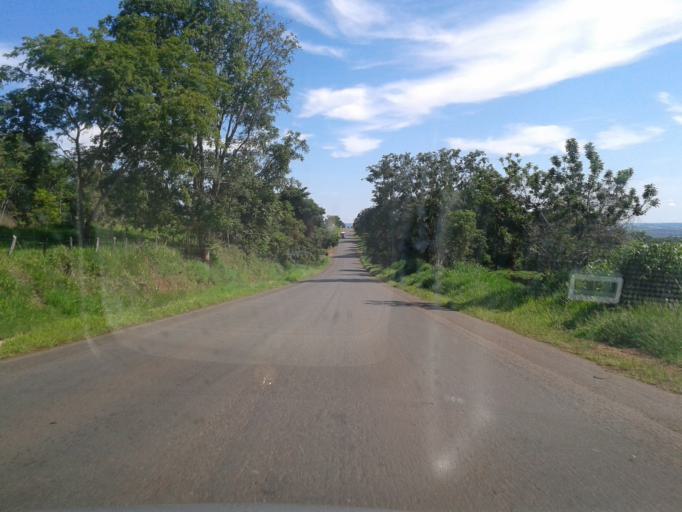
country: BR
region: Goias
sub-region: Piracanjuba
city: Piracanjuba
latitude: -17.2230
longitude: -48.7125
